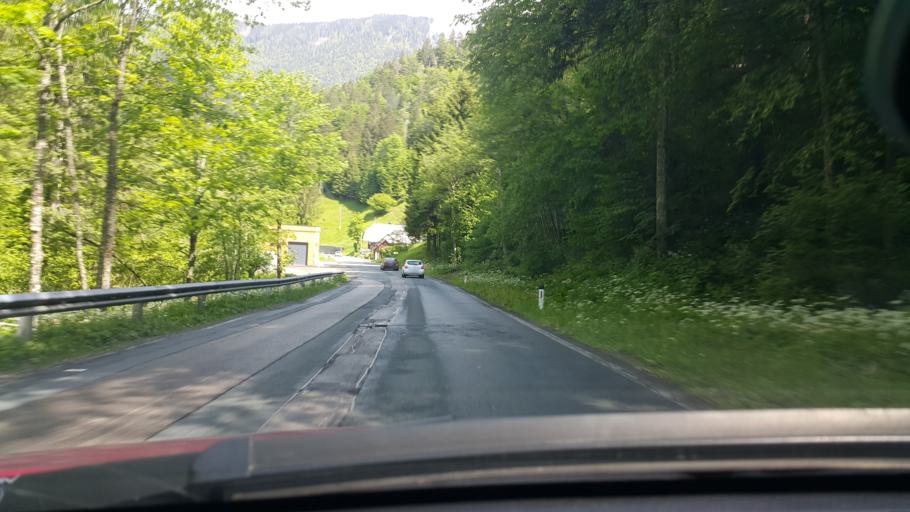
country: AT
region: Carinthia
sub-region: Politischer Bezirk Klagenfurt Land
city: Ferlach
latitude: 46.4735
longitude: 14.2590
